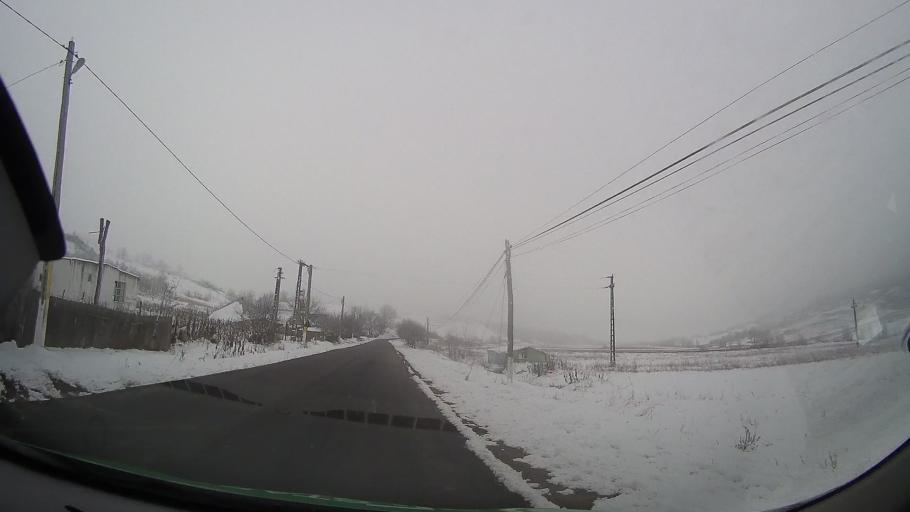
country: RO
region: Bacau
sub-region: Comuna Oncesti
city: Oncesti
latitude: 46.4847
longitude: 27.2555
